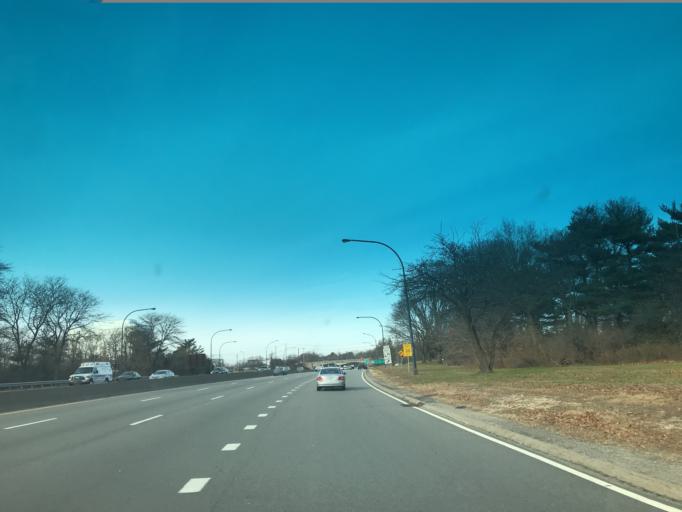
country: US
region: New York
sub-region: Nassau County
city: Carle Place
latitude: 40.7403
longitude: -73.6103
